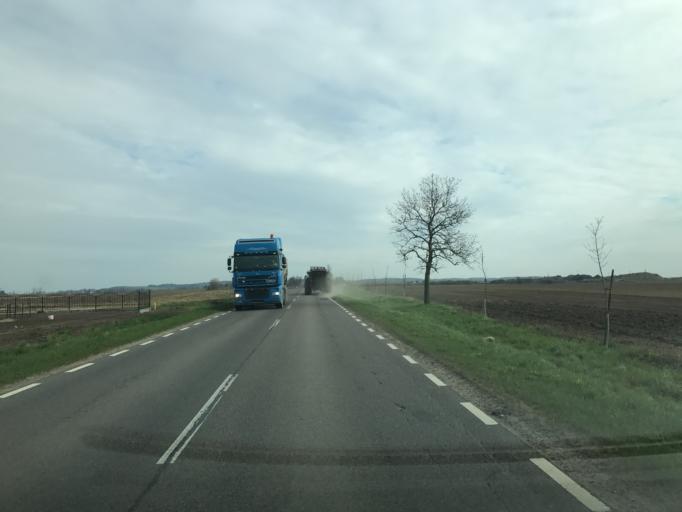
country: PL
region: Warmian-Masurian Voivodeship
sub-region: Powiat ostrodzki
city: Gierzwald
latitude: 53.5136
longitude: 20.0868
